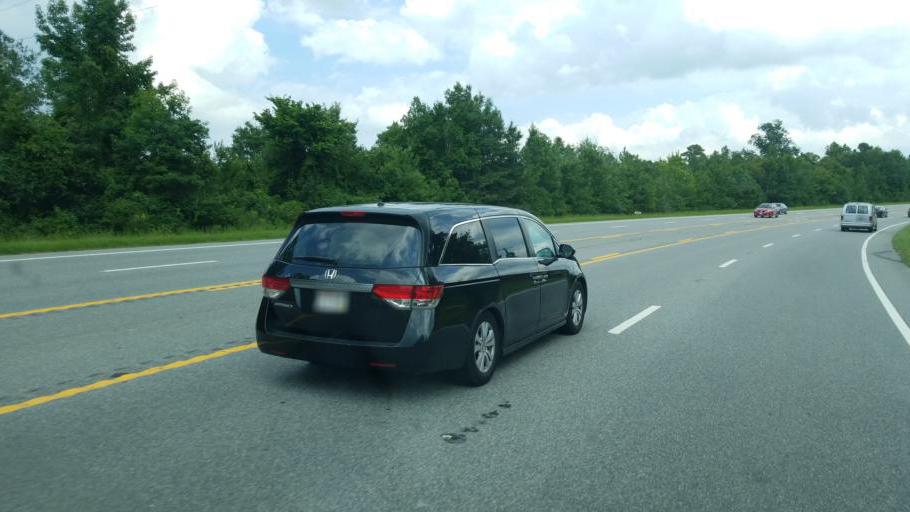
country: US
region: North Carolina
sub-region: Currituck County
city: Moyock
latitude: 36.4969
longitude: -76.1397
